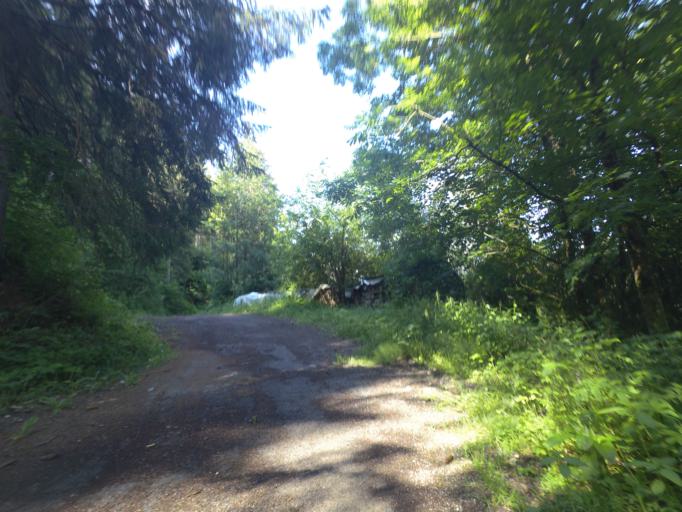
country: AT
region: Salzburg
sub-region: Politischer Bezirk Sankt Johann im Pongau
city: Schwarzach im Pongau
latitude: 47.3103
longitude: 13.1454
